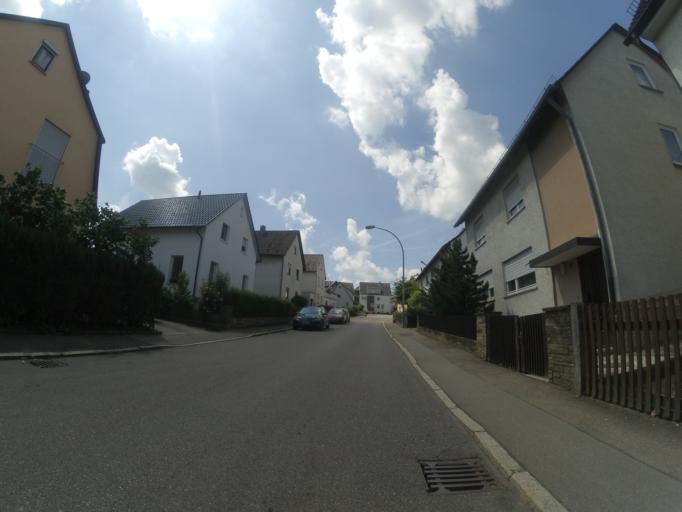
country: DE
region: Baden-Wuerttemberg
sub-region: Tuebingen Region
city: Beimerstetten
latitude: 48.4451
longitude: 9.9921
